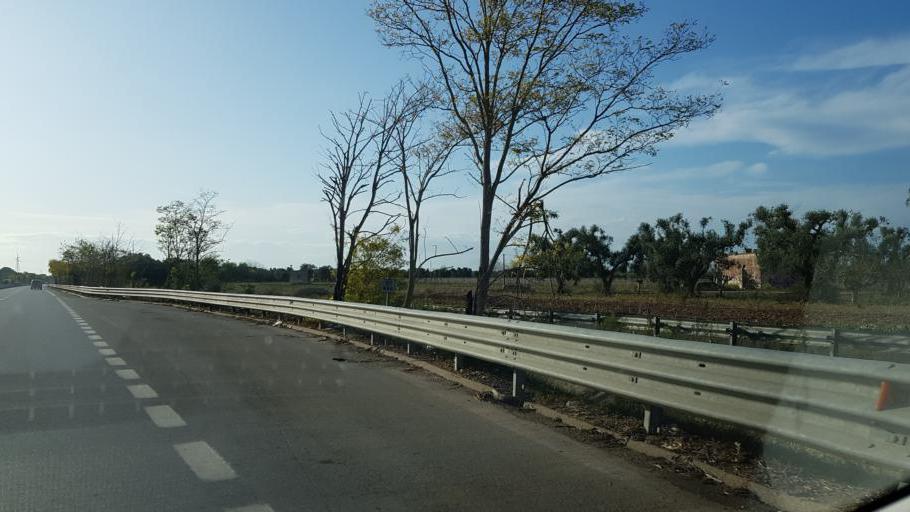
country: IT
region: Apulia
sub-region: Provincia di Brindisi
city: Oria
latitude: 40.5364
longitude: 17.6424
